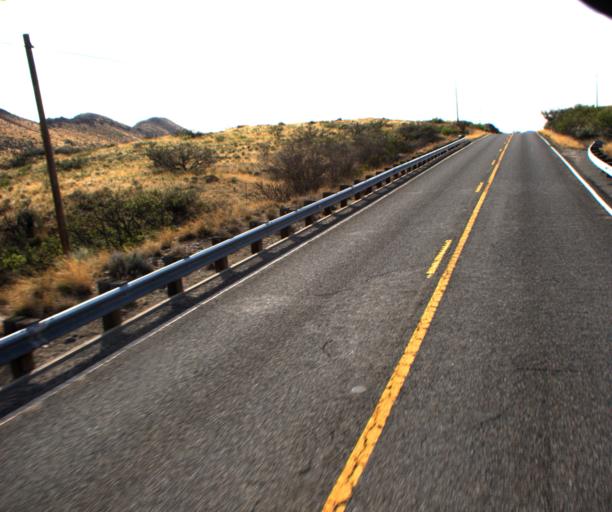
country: US
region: Arizona
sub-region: Cochise County
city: Willcox
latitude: 32.1718
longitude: -109.5995
